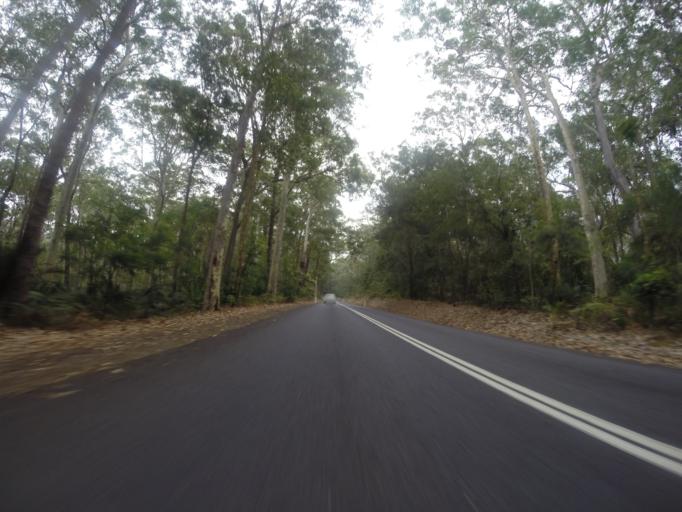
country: AU
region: New South Wales
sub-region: Eurobodalla
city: Batemans Bay
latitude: -35.6578
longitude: 150.2931
